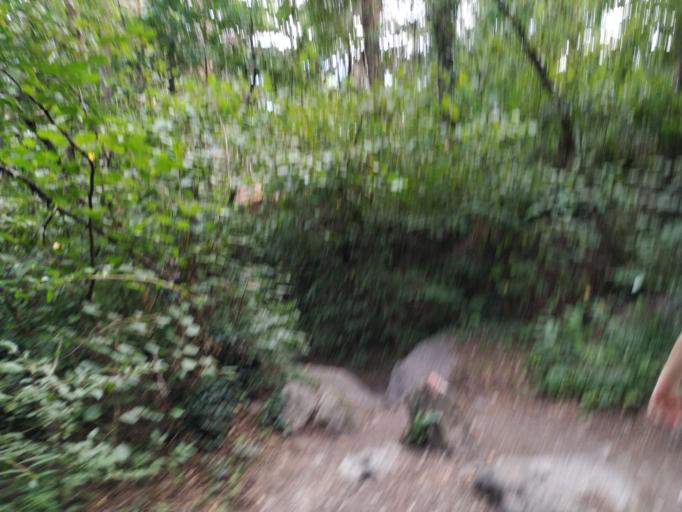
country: IT
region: Trentino-Alto Adige
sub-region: Bolzano
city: Parcines
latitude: 46.6810
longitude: 11.0649
